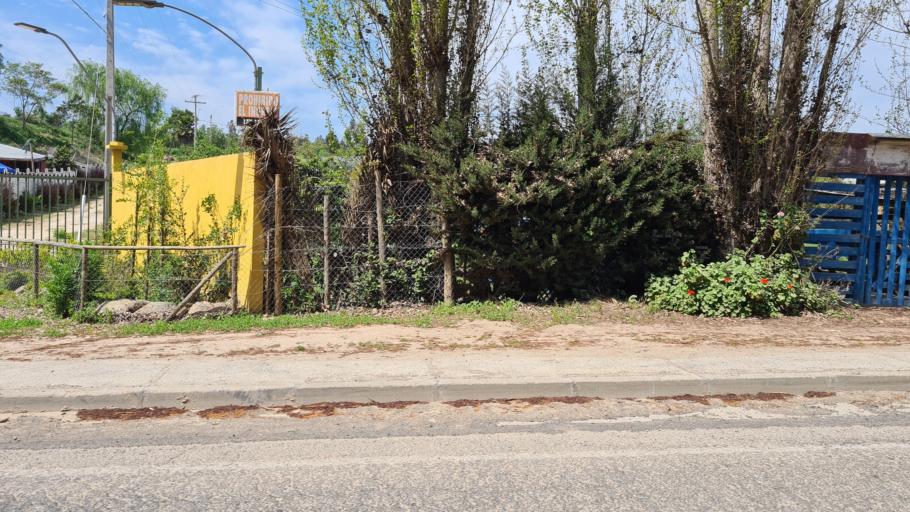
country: CL
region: O'Higgins
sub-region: Provincia de Cachapoal
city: San Vicente
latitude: -34.1588
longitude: -71.4260
